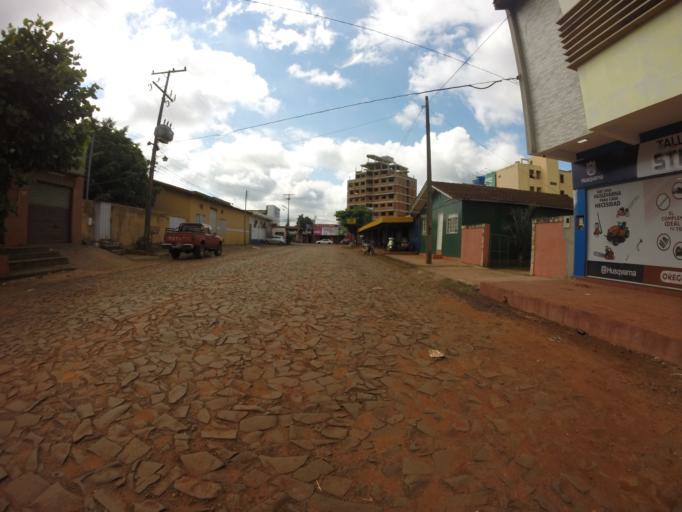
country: PY
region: Alto Parana
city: Ciudad del Este
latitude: -25.3960
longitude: -54.6404
